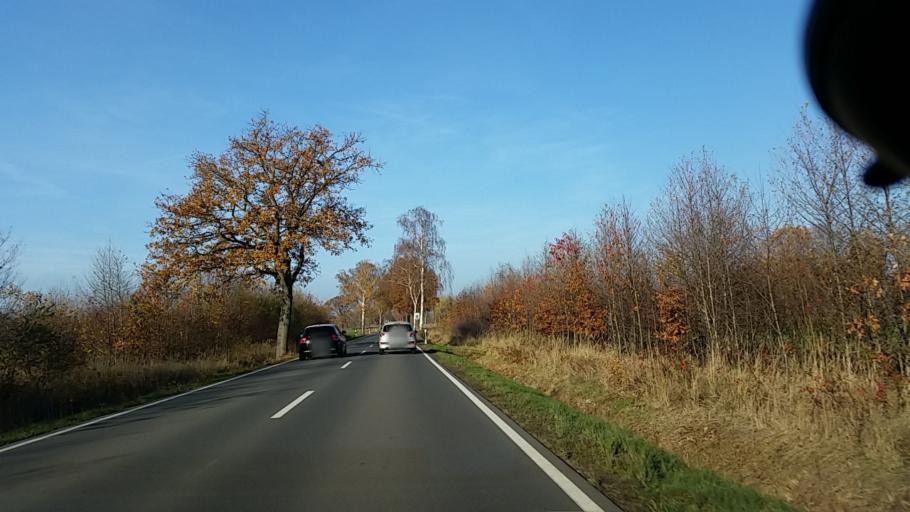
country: DE
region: Lower Saxony
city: Tiddische
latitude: 52.4862
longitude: 10.8126
